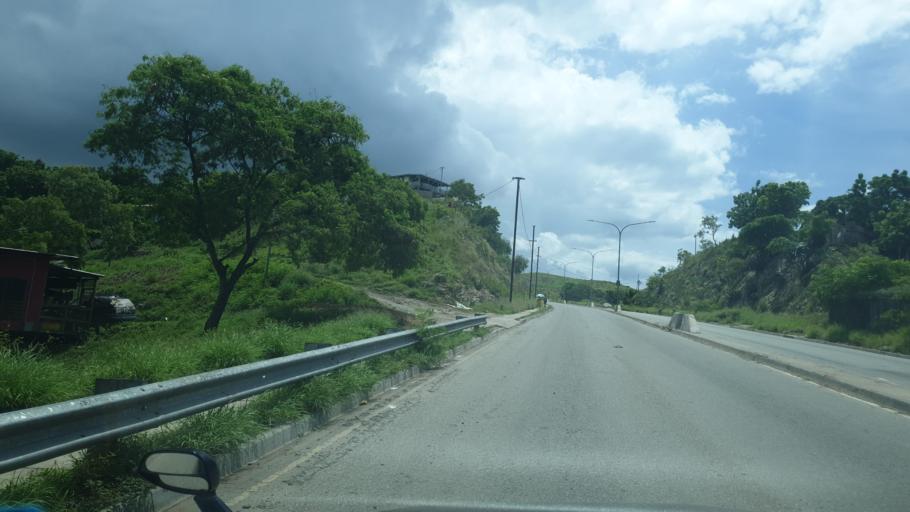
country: PG
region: National Capital
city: Port Moresby
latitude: -9.4512
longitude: 147.1538
